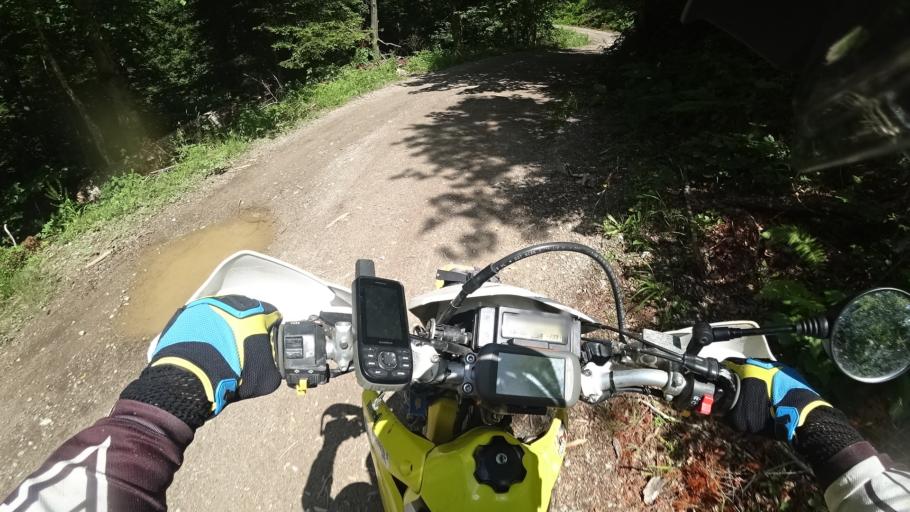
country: HR
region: Primorsko-Goranska
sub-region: Grad Delnice
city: Delnice
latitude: 45.4491
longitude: 14.7404
